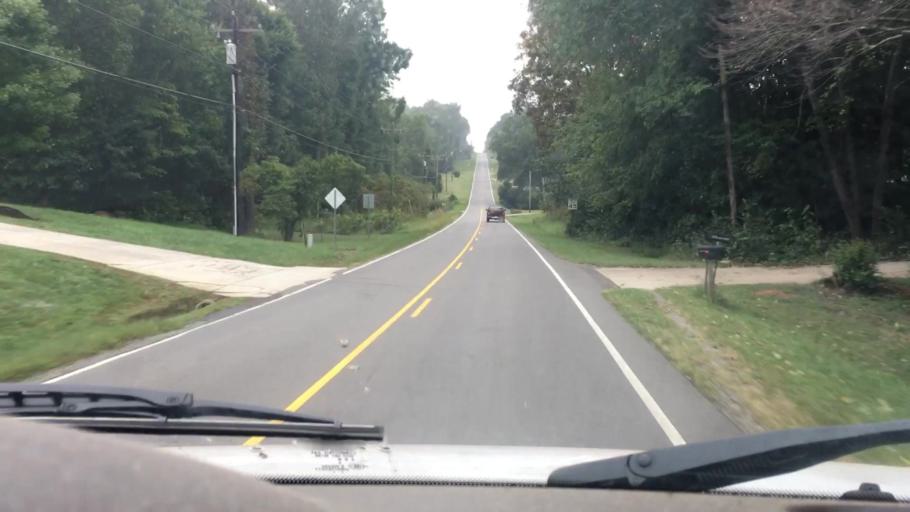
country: US
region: North Carolina
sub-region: Iredell County
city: Mooresville
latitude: 35.6363
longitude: -80.7760
